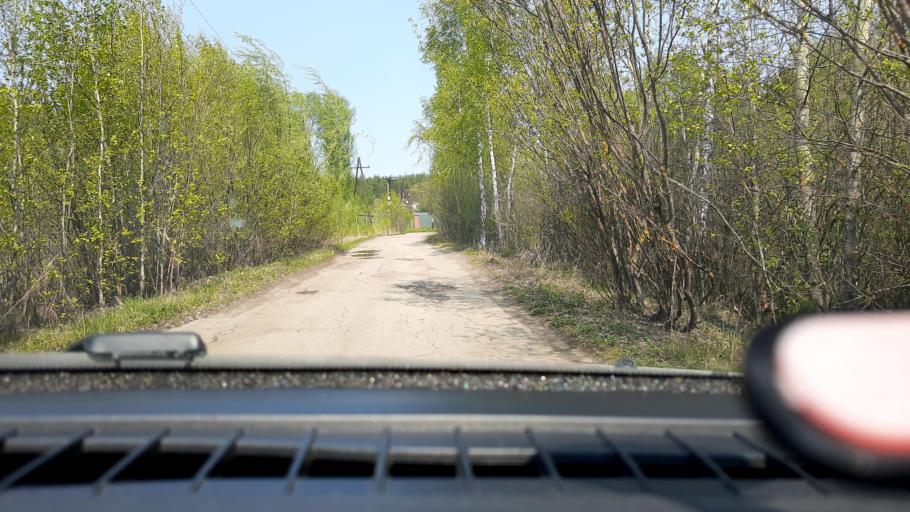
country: RU
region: Nizjnij Novgorod
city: Gorbatovka
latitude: 56.2711
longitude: 43.7973
